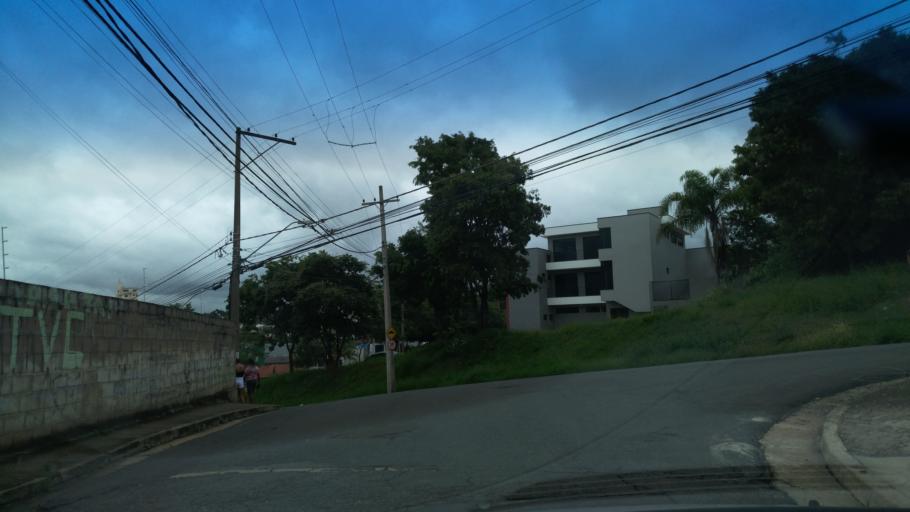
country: BR
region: Sao Paulo
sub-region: Valinhos
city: Valinhos
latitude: -22.9610
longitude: -47.0043
